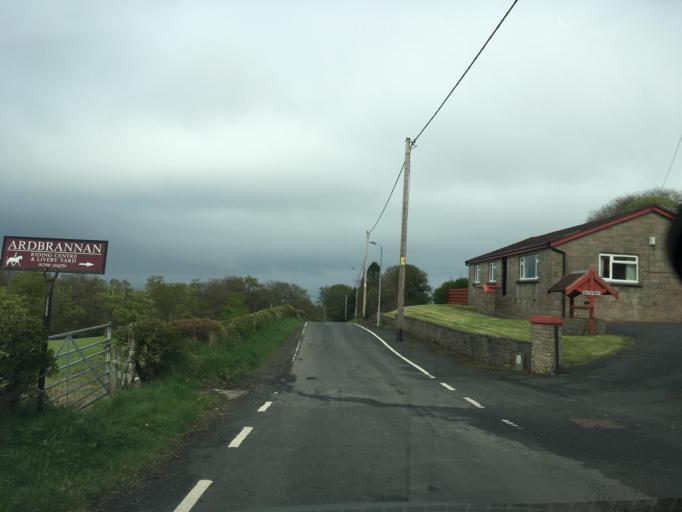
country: GB
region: Scotland
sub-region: Argyll and Bute
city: Rothesay
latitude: 55.8390
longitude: -5.0323
